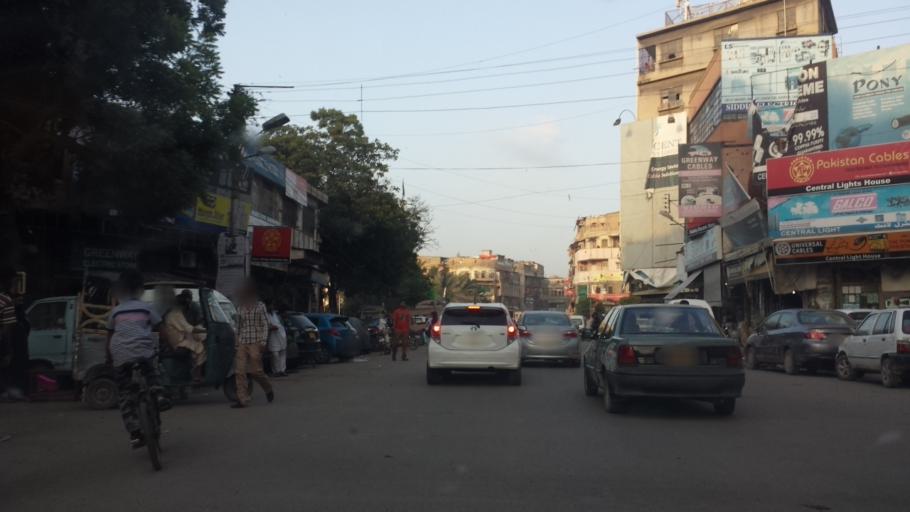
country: PK
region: Sindh
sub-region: Karachi District
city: Karachi
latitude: 24.8553
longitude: 67.0125
